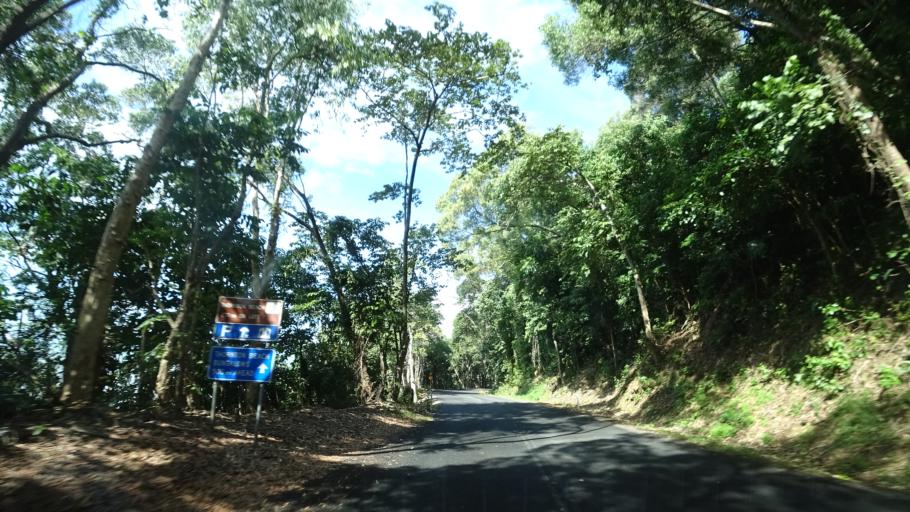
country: AU
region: Queensland
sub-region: Cairns
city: Port Douglas
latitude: -16.1672
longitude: 145.4434
